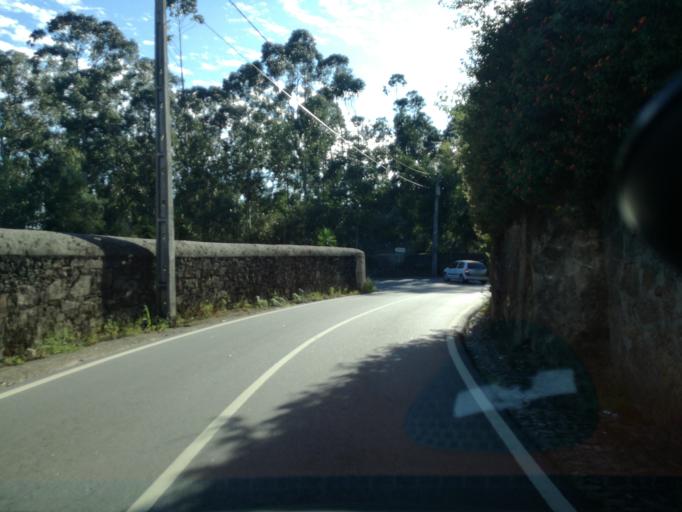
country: PT
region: Porto
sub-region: Santo Tirso
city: Sao Miguel do Couto
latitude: 41.3041
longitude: -8.4557
